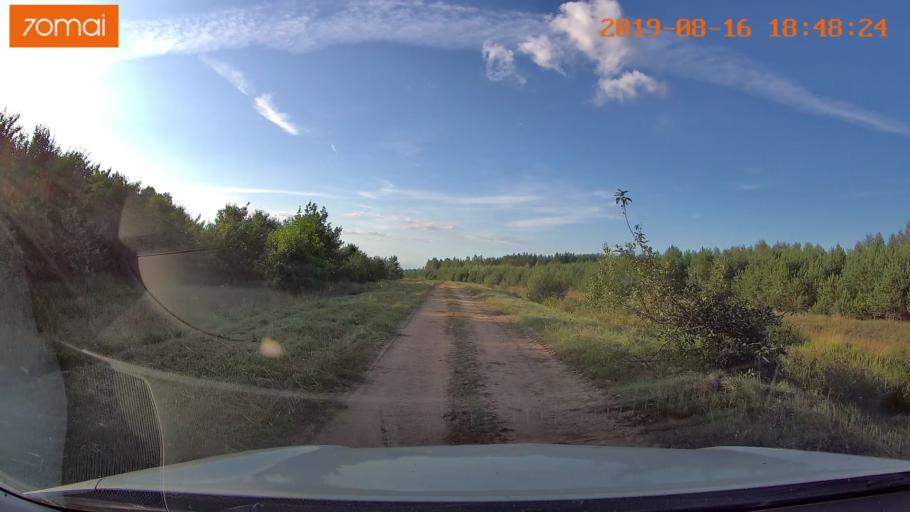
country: BY
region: Mogilev
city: Asipovichy
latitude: 53.2328
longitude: 28.6688
